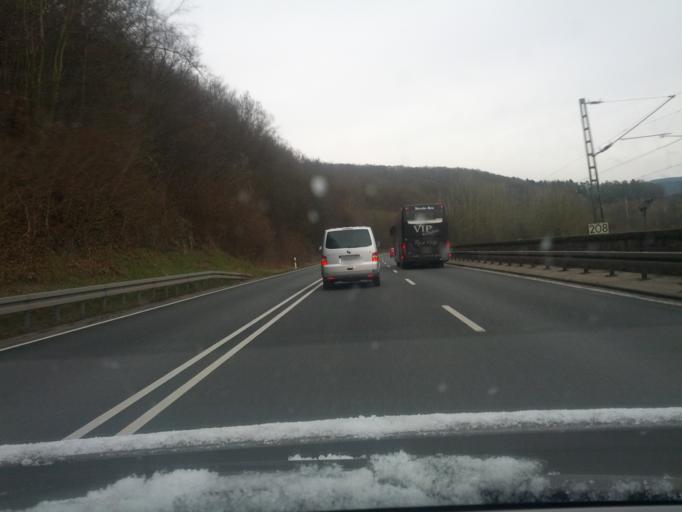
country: DE
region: Hesse
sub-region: Regierungsbezirk Kassel
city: Bad Sooden-Allendorf
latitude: 51.2449
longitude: 9.9824
